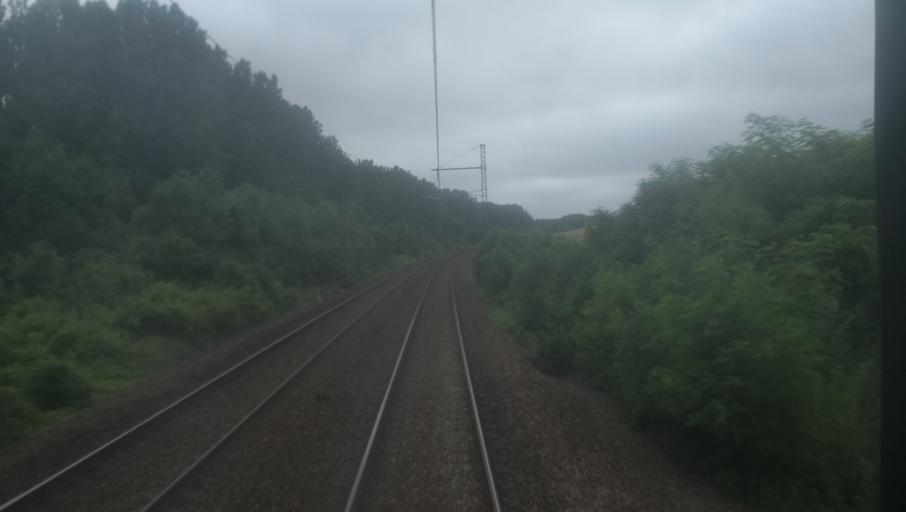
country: FR
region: Centre
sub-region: Departement de l'Indre
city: Sainte-Lizaigne
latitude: 47.0457
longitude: 2.0327
